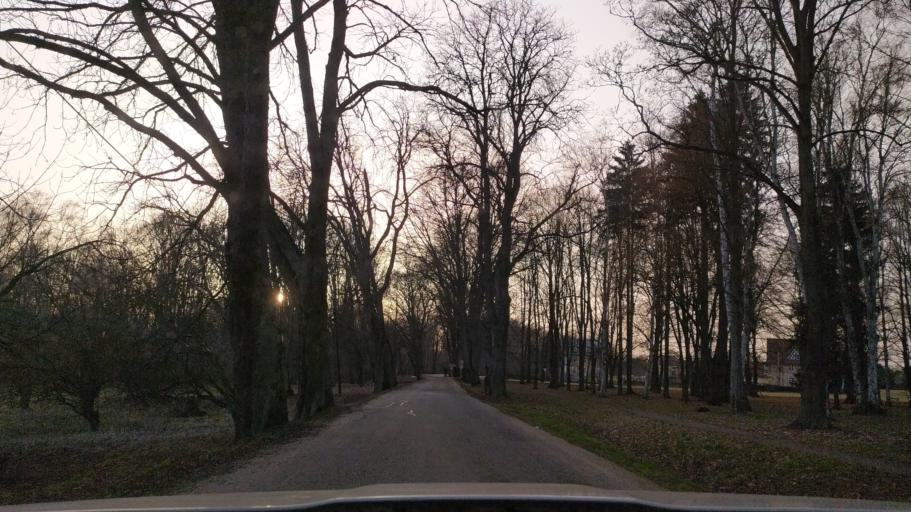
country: CZ
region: Karlovarsky
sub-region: Okres Cheb
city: Frantiskovy Lazne
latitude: 50.1150
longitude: 12.3658
